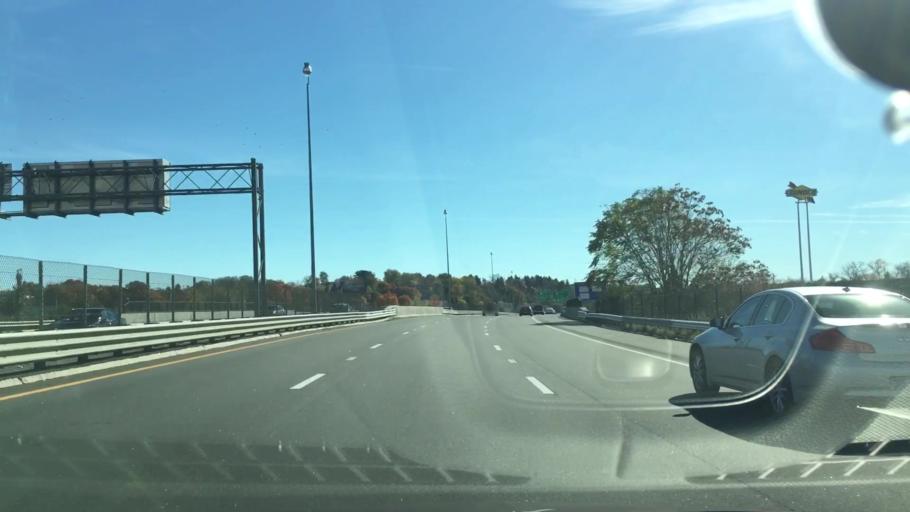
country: US
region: Massachusetts
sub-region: Hampden County
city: Springfield
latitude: 42.0930
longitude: -72.5831
